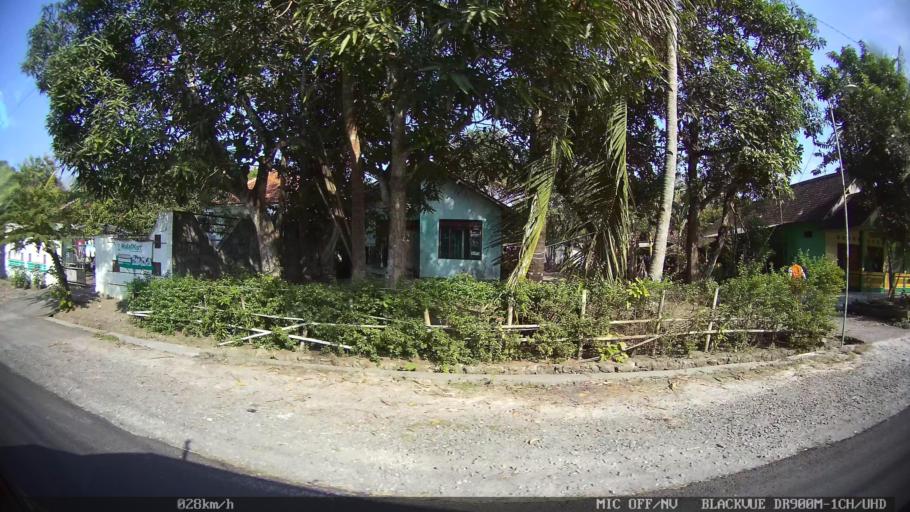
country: ID
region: Daerah Istimewa Yogyakarta
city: Godean
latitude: -7.8157
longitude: 110.2754
